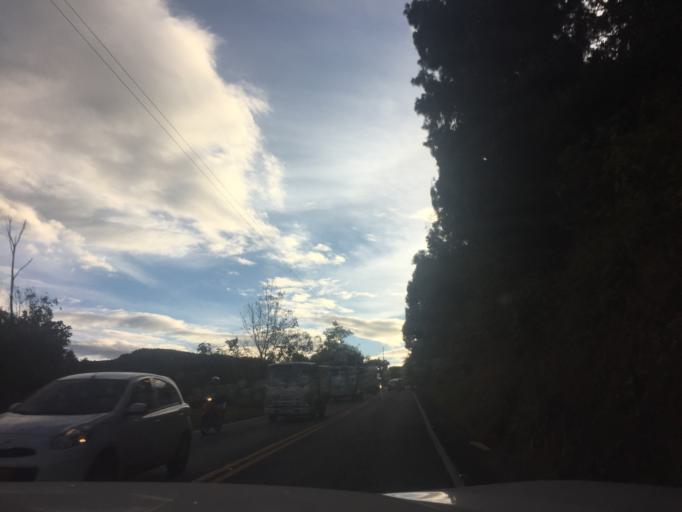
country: CO
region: Narino
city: Pasto
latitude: 1.2593
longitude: -77.2895
